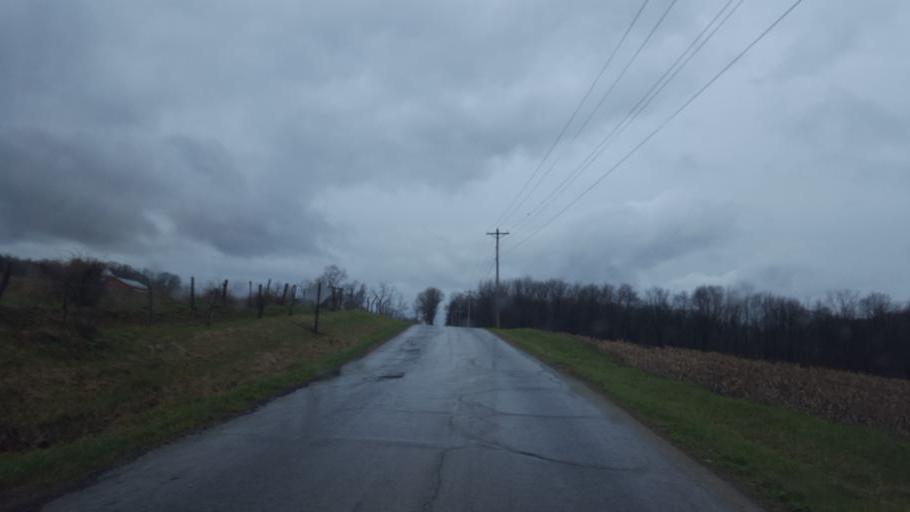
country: US
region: Ohio
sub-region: Sandusky County
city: Bellville
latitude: 40.5759
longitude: -82.6049
